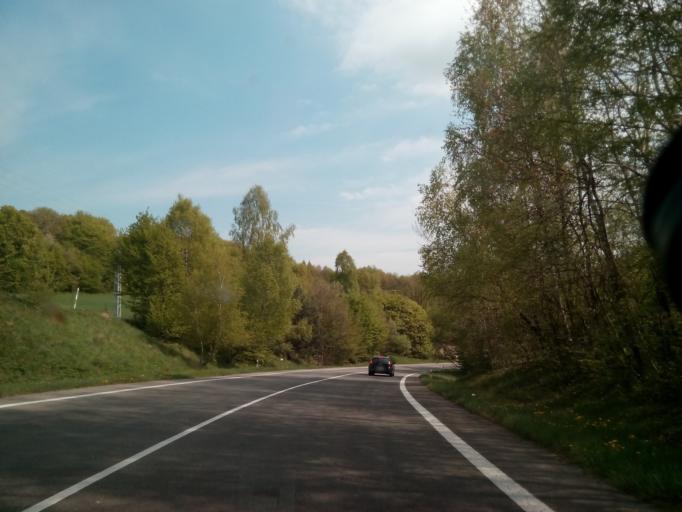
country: SK
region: Presovsky
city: Giraltovce
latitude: 49.0500
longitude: 21.4240
